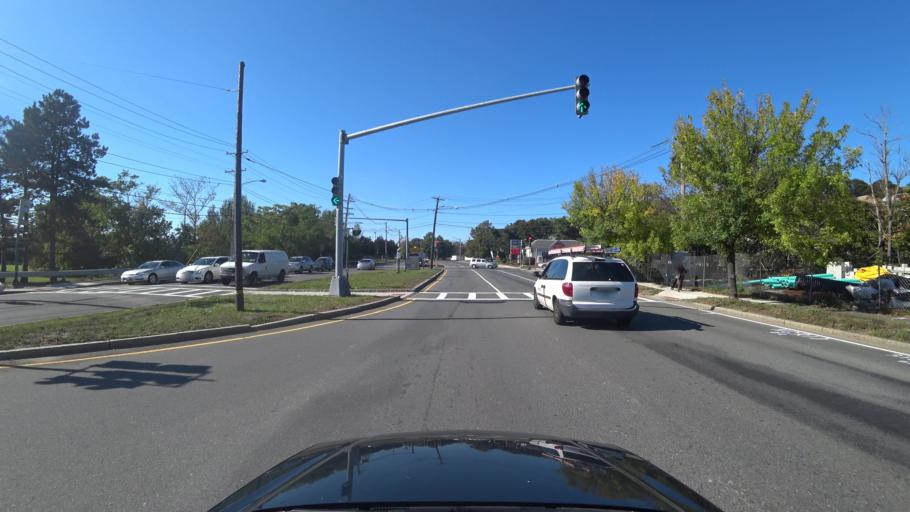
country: US
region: Massachusetts
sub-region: Suffolk County
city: Revere
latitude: 42.4007
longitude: -70.9968
